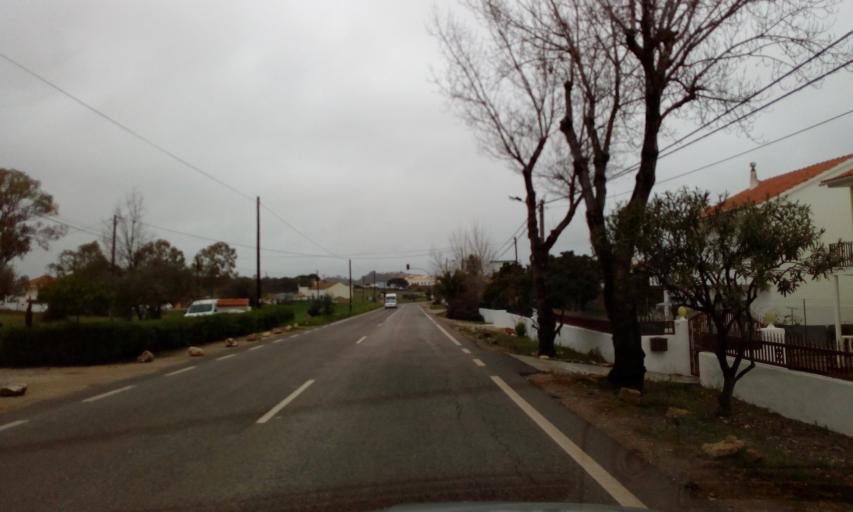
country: PT
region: Faro
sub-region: Albufeira
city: Guia
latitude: 37.1554
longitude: -8.2838
